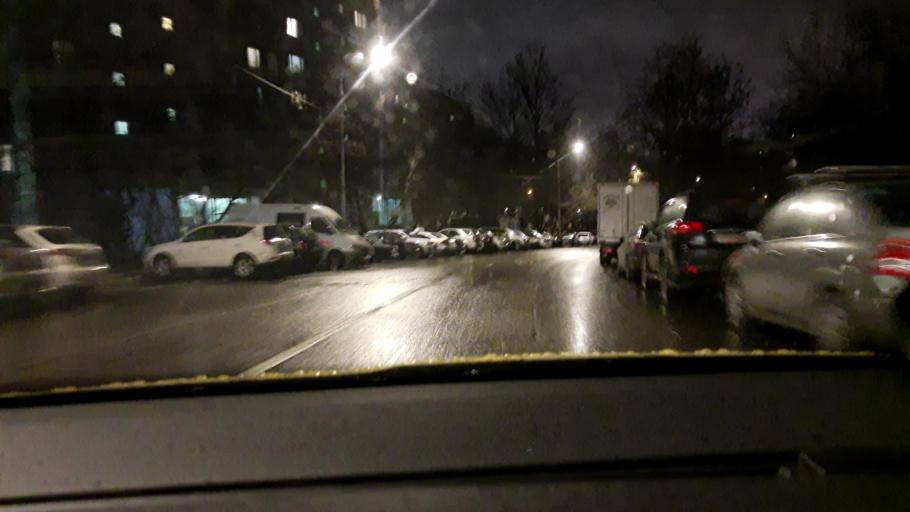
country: RU
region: Moscow
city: Strogino
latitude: 55.8419
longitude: 37.4200
